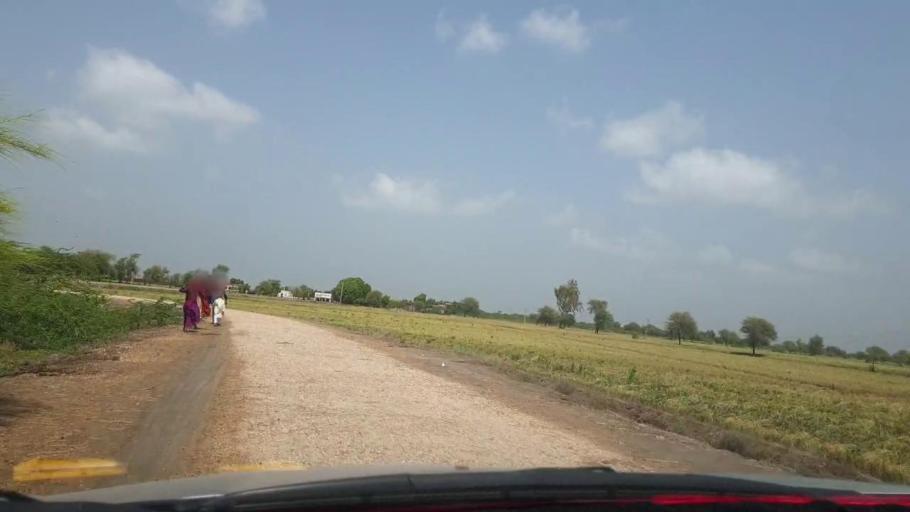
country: PK
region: Sindh
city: Rajo Khanani
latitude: 24.9295
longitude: 68.8991
